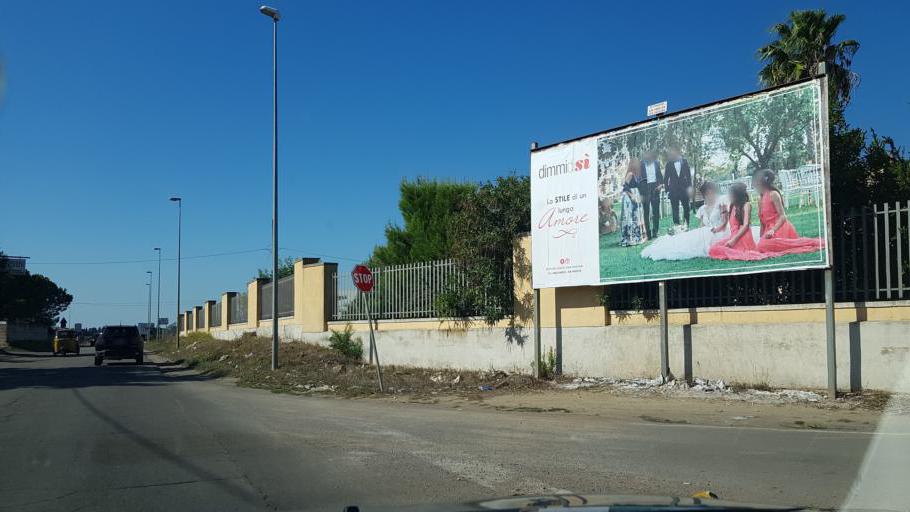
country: IT
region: Apulia
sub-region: Provincia di Lecce
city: Leverano
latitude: 40.2947
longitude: 17.9885
